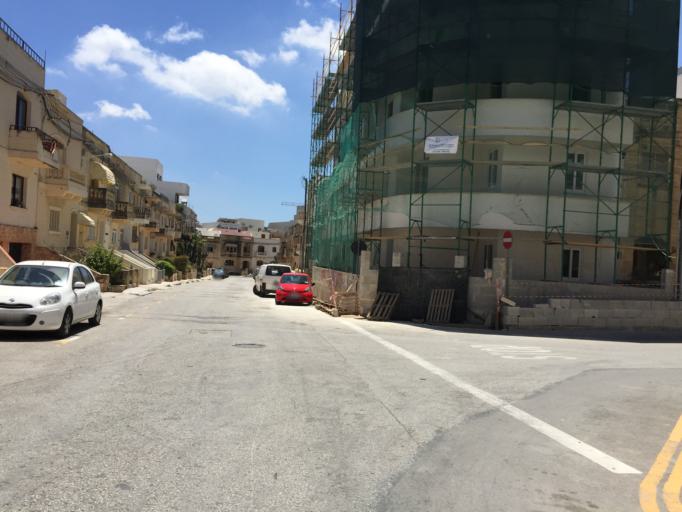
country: MT
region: Is-Swieqi
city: Swieqi
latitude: 35.9213
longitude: 14.4823
